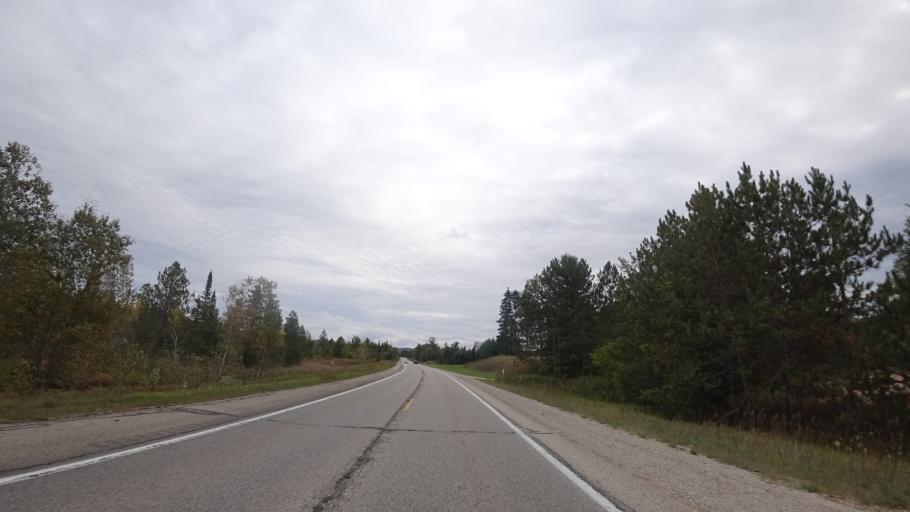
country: US
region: Michigan
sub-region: Charlevoix County
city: Boyne City
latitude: 45.2005
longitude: -84.9237
